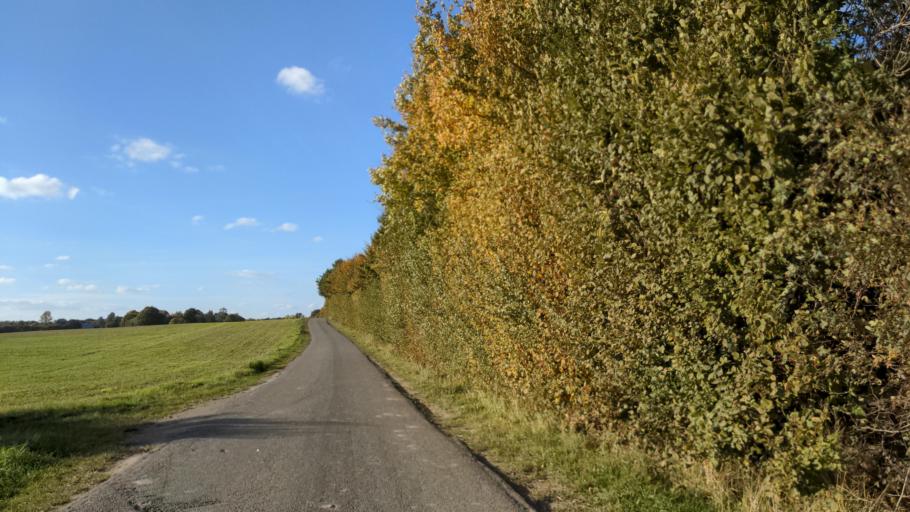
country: DE
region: Schleswig-Holstein
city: Monkhagen
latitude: 53.9197
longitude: 10.5435
